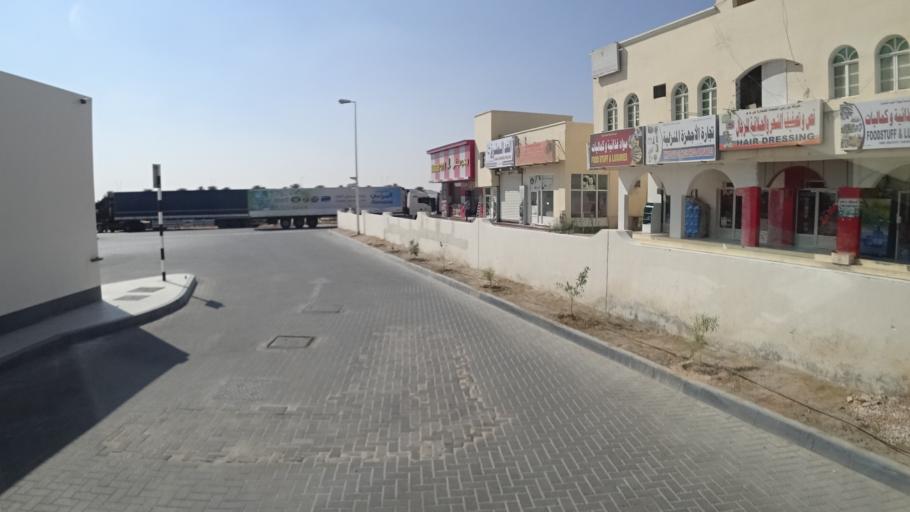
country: OM
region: Zufar
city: Salalah
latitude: 17.6111
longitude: 54.0354
